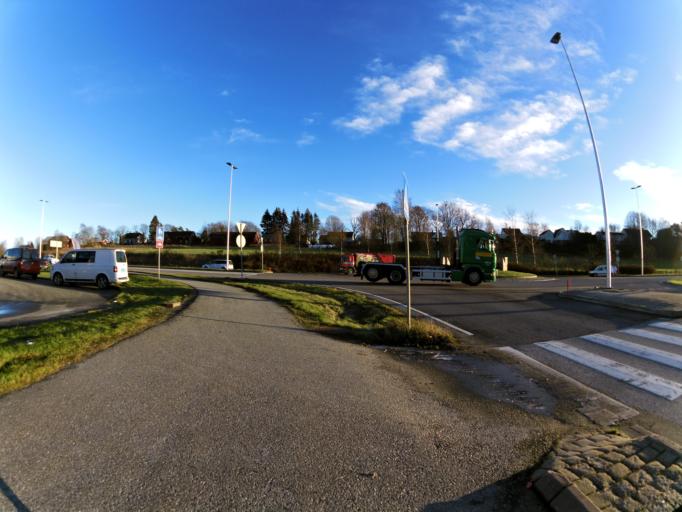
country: NO
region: Ostfold
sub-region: Fredrikstad
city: Fredrikstad
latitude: 59.2379
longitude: 10.9669
